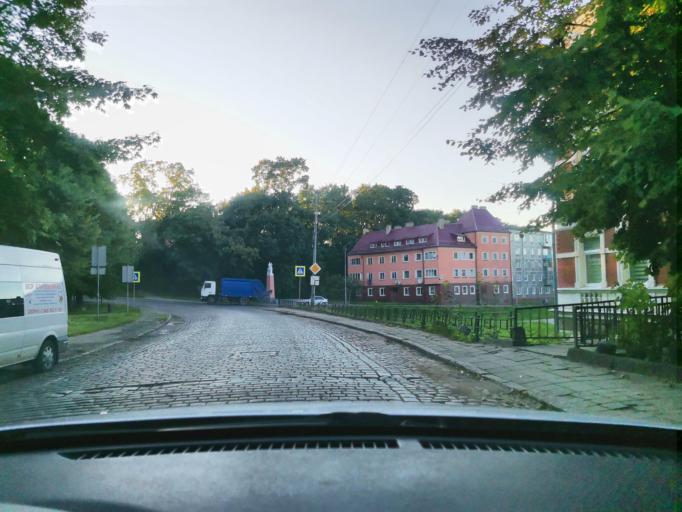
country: RU
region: Kaliningrad
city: Chernyakhovsk
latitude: 54.6393
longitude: 21.8085
